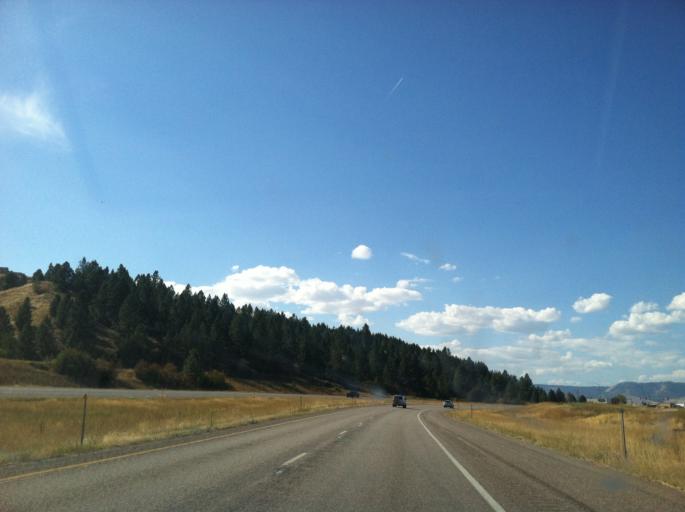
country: US
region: Montana
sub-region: Lake County
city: Polson
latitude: 47.6791
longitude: -114.1147
